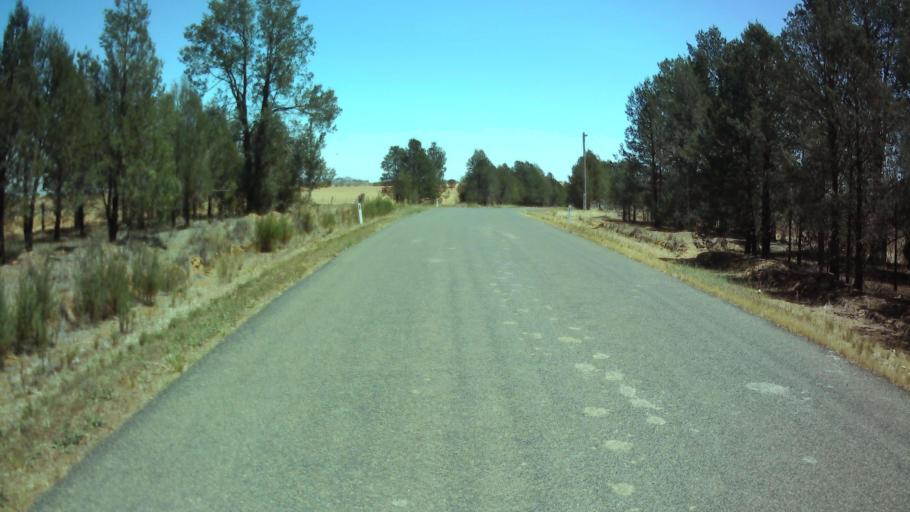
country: AU
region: New South Wales
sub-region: Weddin
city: Grenfell
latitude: -34.0506
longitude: 148.1915
